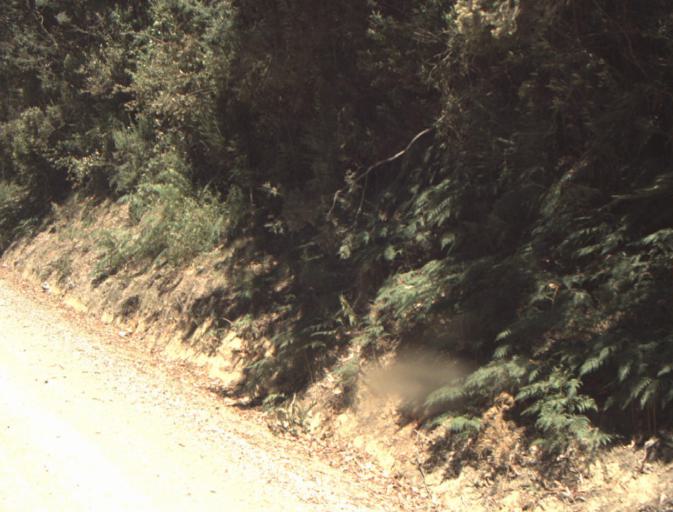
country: AU
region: Tasmania
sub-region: Dorset
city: Scottsdale
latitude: -41.3232
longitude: 147.4191
